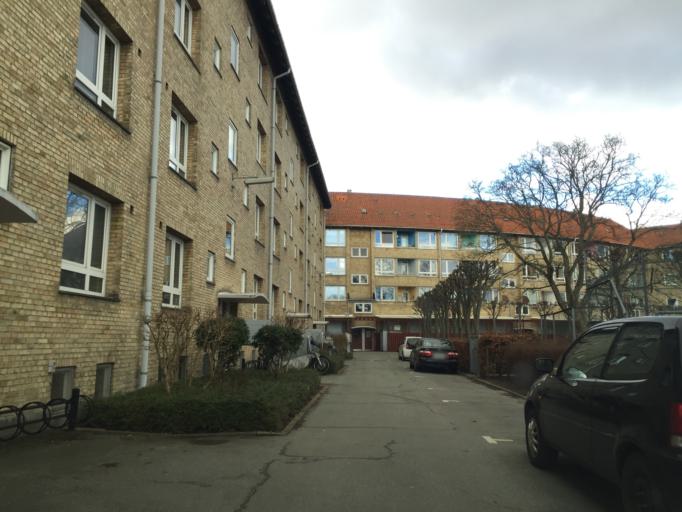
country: DK
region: Capital Region
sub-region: Frederiksberg Kommune
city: Frederiksberg
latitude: 55.6479
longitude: 12.5347
